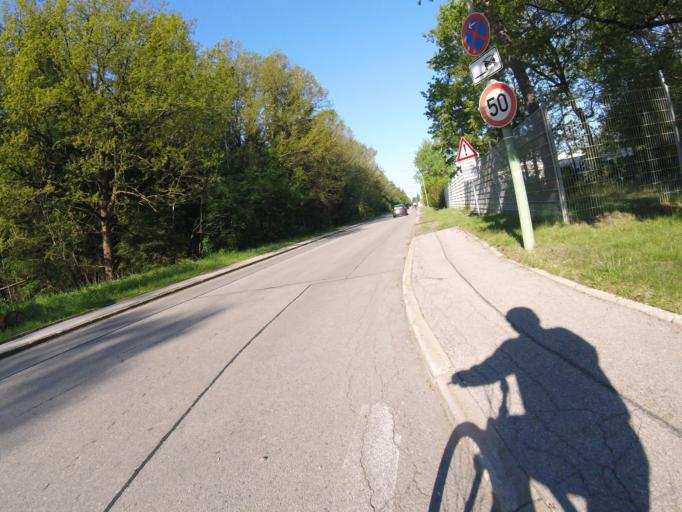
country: DE
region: Bavaria
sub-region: Upper Bavaria
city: Ottobrunn
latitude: 48.0498
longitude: 11.6625
